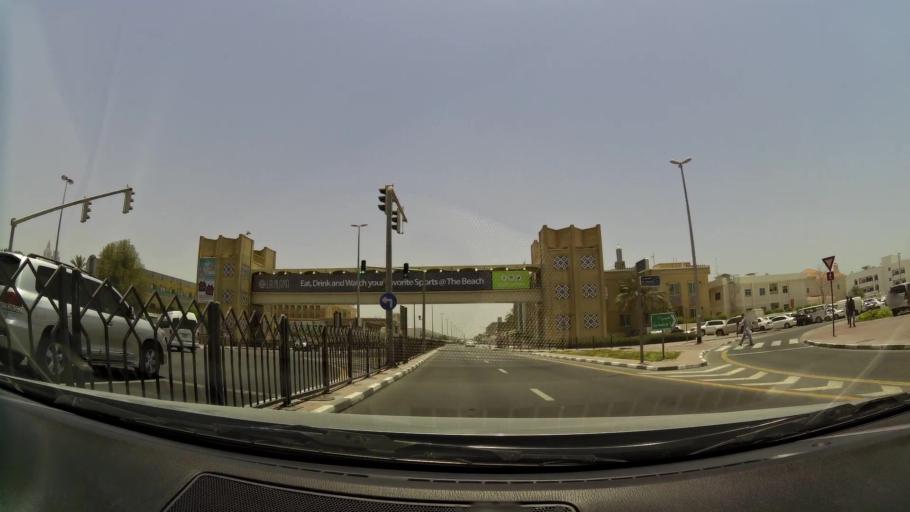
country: AE
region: Ash Shariqah
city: Sharjah
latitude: 25.2317
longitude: 55.2688
